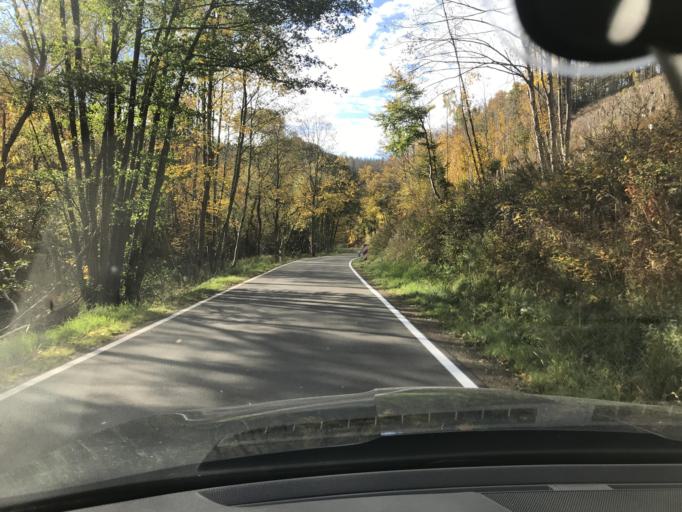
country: DE
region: Saxony-Anhalt
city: Friedrichsbrunn
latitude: 51.6886
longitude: 10.9622
